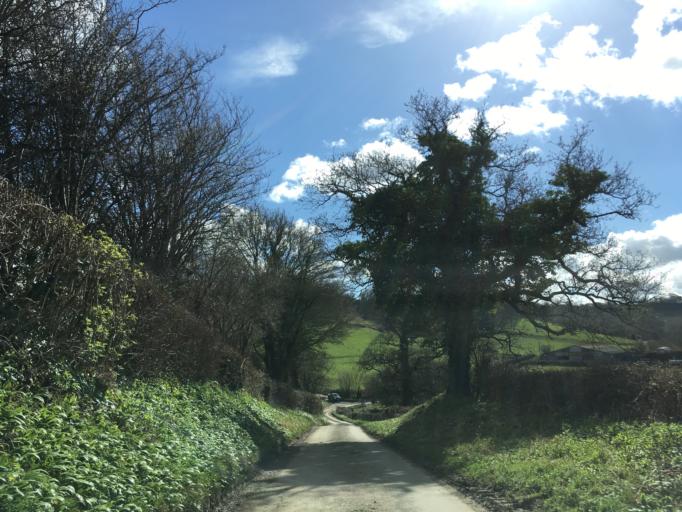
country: GB
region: England
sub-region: South Gloucestershire
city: Horton
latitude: 51.5741
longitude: -2.3389
